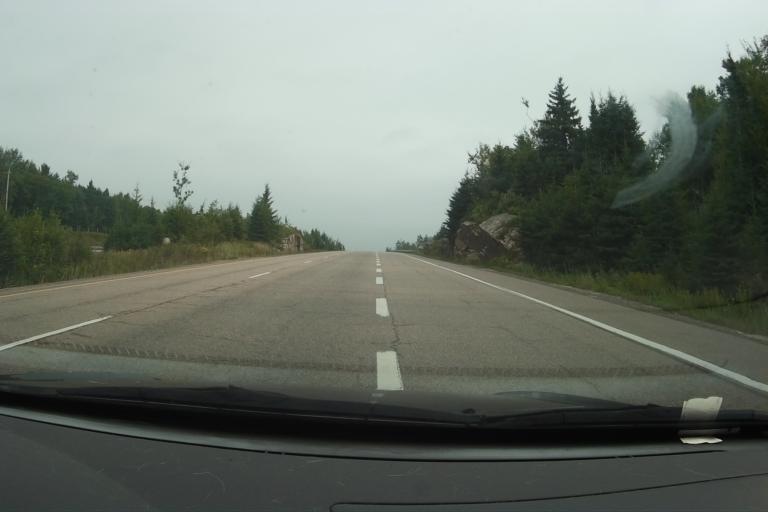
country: CA
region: Ontario
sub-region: Nipissing District
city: North Bay
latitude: 46.2007
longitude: -79.3526
